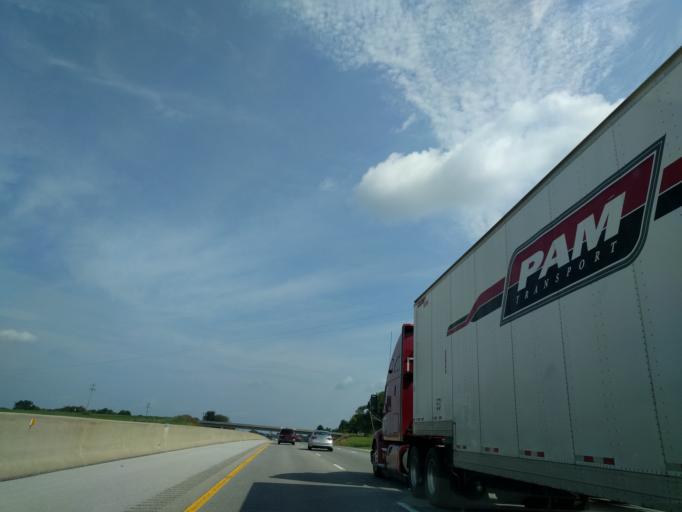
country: US
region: Kentucky
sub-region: Warren County
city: Plano
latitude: 36.7921
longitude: -86.4751
